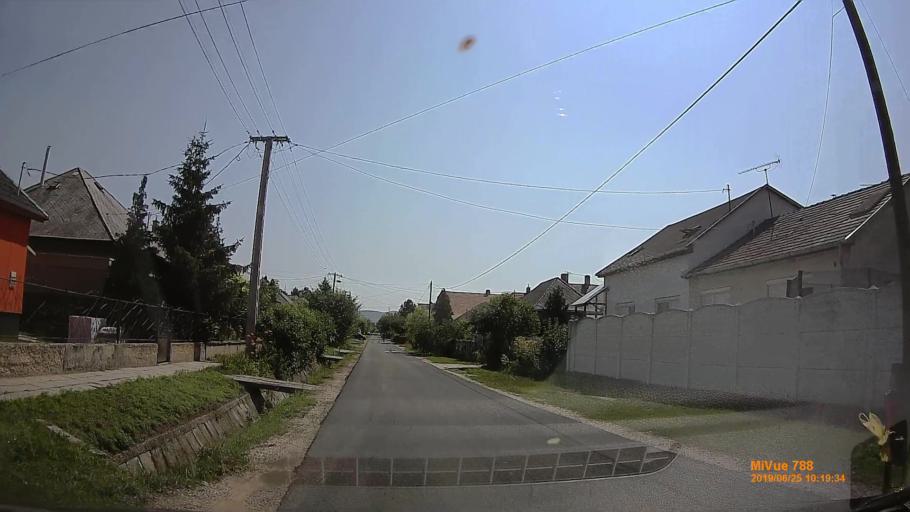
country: HU
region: Komarom-Esztergom
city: Tokod
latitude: 47.7362
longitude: 18.6966
